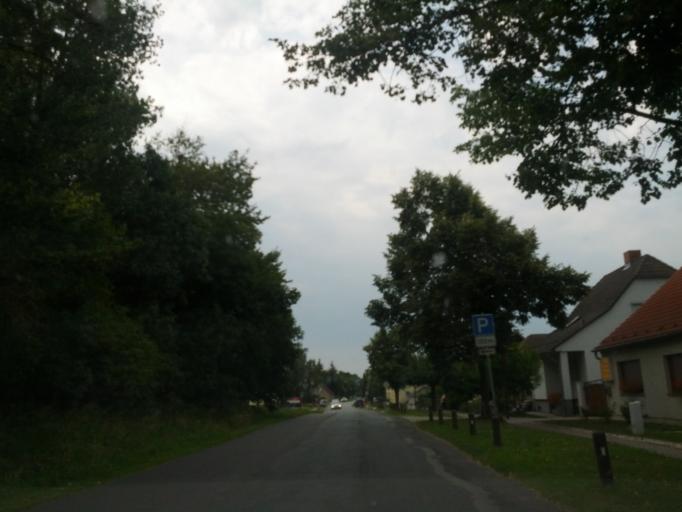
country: DE
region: Brandenburg
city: Kremmen
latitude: 52.7554
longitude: 12.8903
